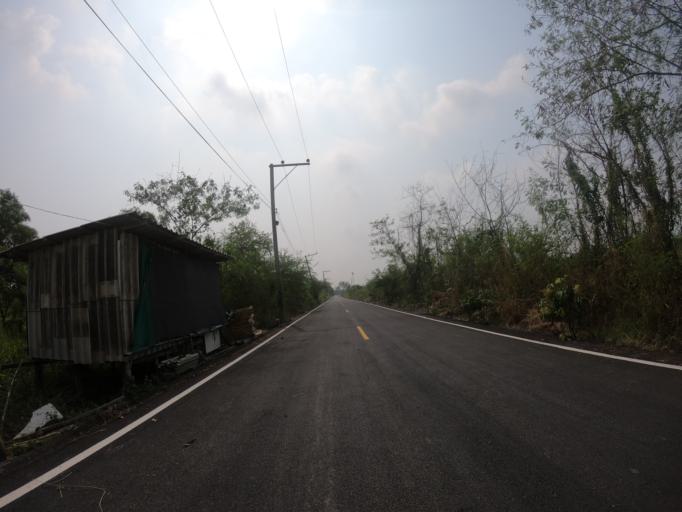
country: TH
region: Pathum Thani
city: Nong Suea
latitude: 14.0650
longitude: 100.8493
